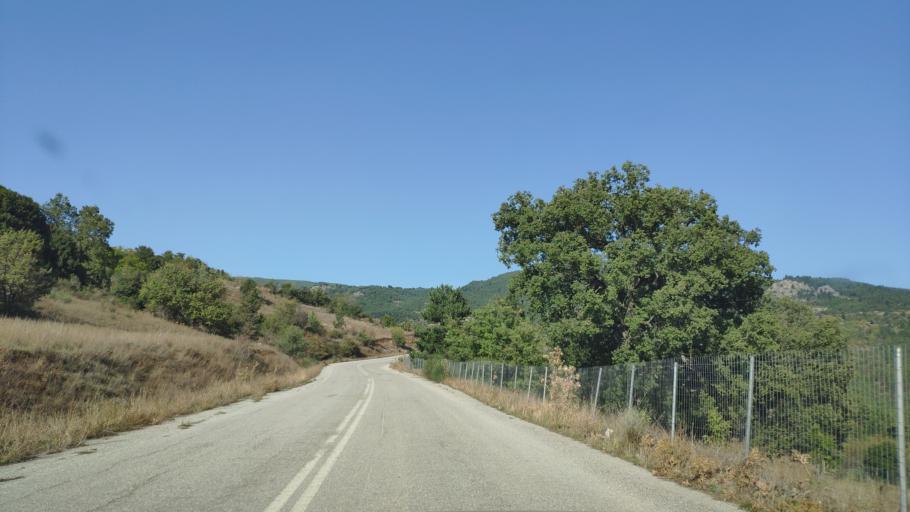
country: GR
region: West Greece
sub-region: Nomos Achaias
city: Aiyira
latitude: 38.0062
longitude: 22.3992
